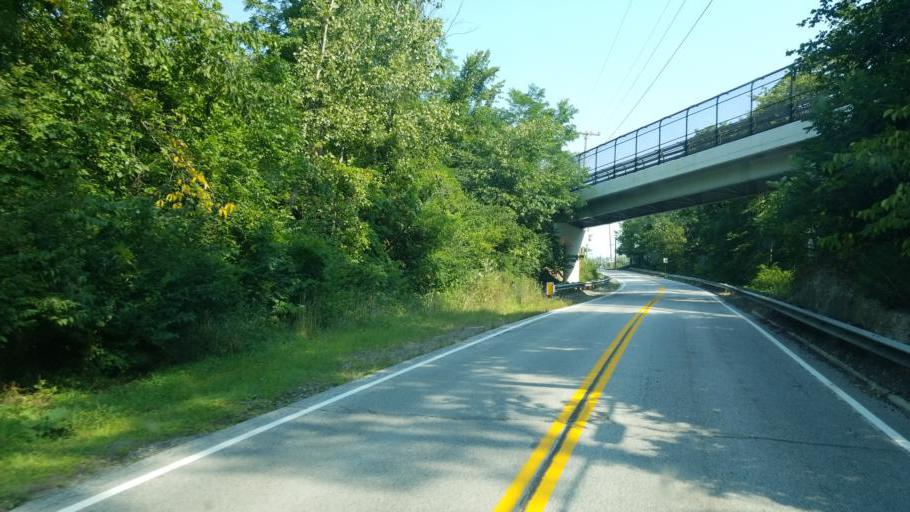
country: US
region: Ohio
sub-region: Lake County
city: Painesville
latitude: 41.7049
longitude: -81.2391
